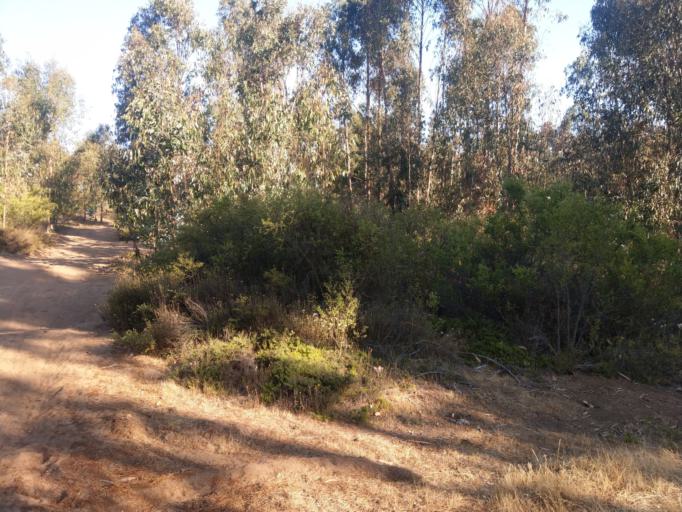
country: CL
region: Valparaiso
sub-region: Provincia de Valparaiso
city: Vina del Mar
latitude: -32.9505
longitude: -71.5232
